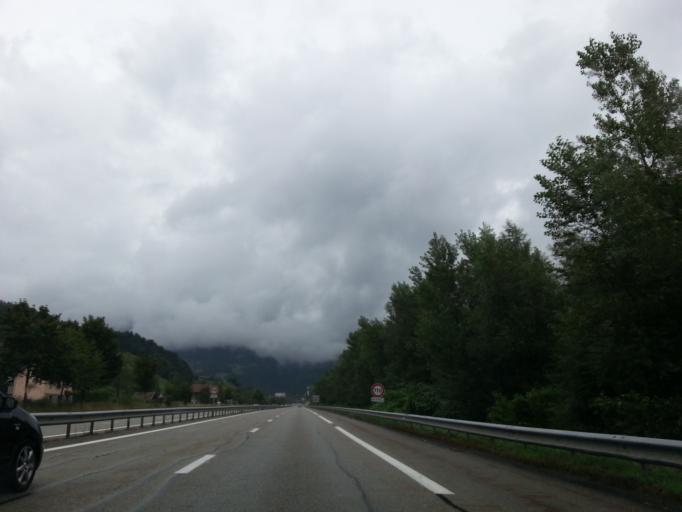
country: FR
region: Rhone-Alpes
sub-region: Departement de la Savoie
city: Marthod
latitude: 45.7228
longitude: 6.4126
